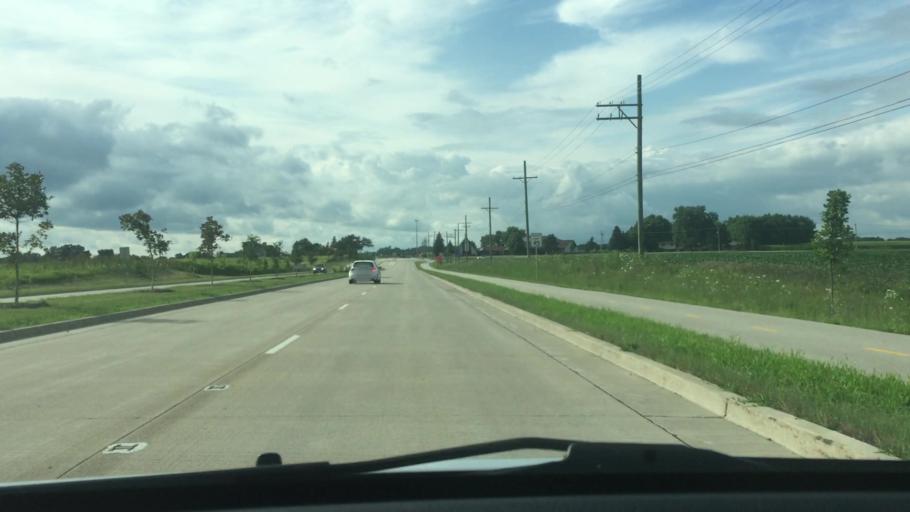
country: US
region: Illinois
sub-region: McHenry County
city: Lakewood
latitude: 42.2643
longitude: -88.3758
